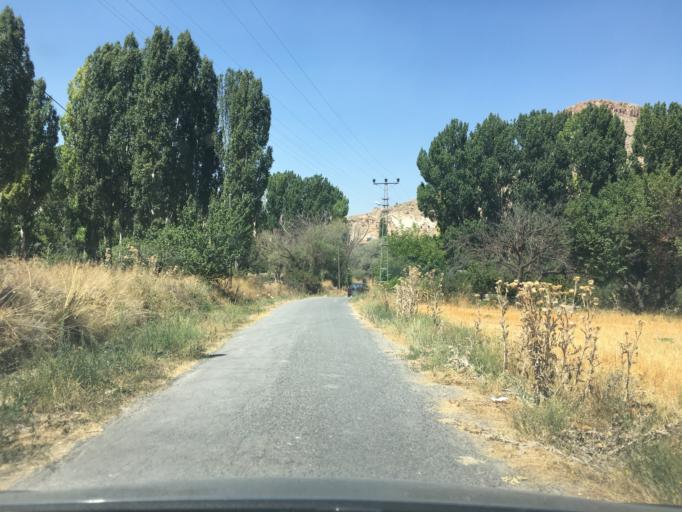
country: TR
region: Nevsehir
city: Urgub
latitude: 38.4692
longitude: 34.9608
